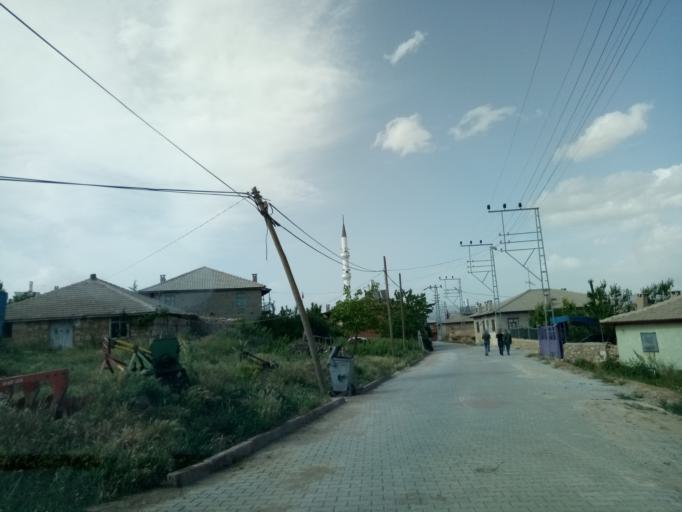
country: TR
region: Konya
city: Ahirli
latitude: 37.2860
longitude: 32.1790
